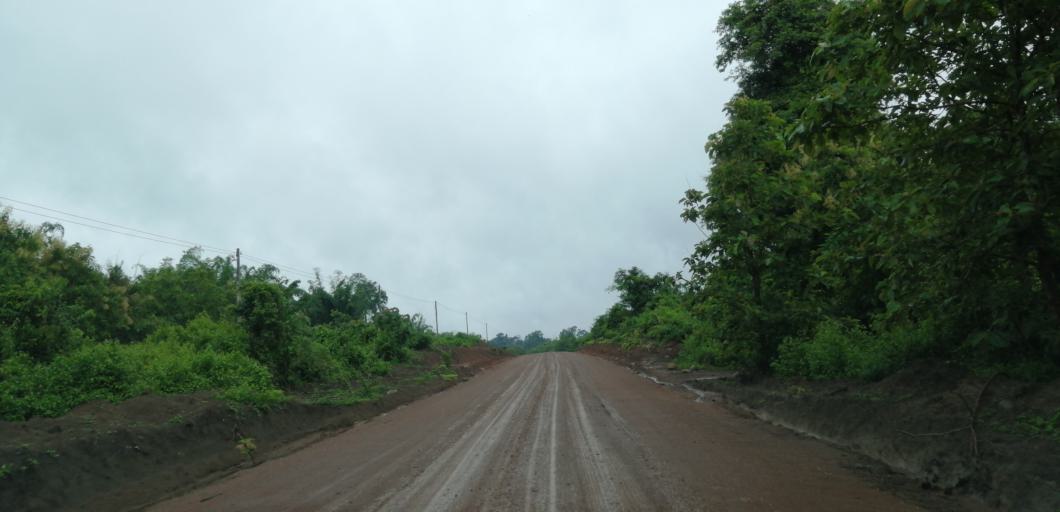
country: LA
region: Attapu
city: Attapu
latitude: 14.7168
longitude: 106.3674
